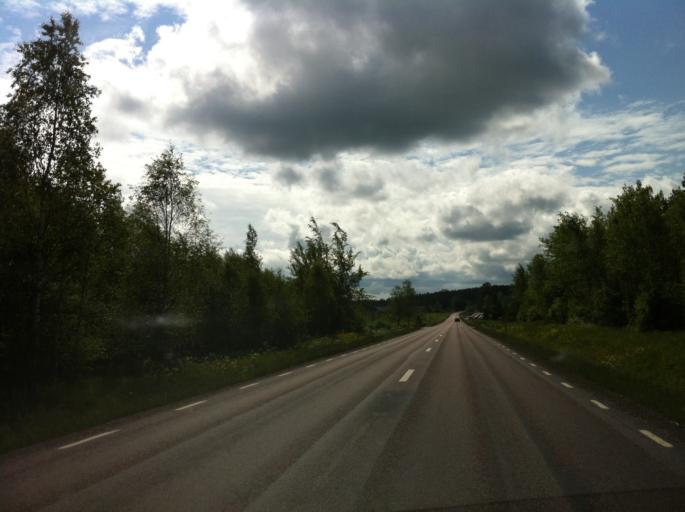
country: SE
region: Vaermland
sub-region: Karlstads Kommun
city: Edsvalla
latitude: 59.6051
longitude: 13.1578
